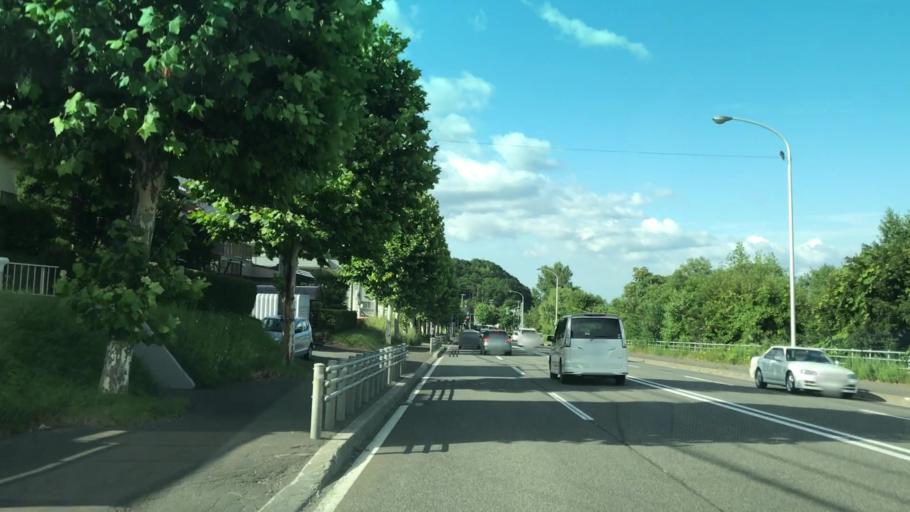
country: JP
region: Hokkaido
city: Sapporo
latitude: 42.9840
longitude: 141.3474
